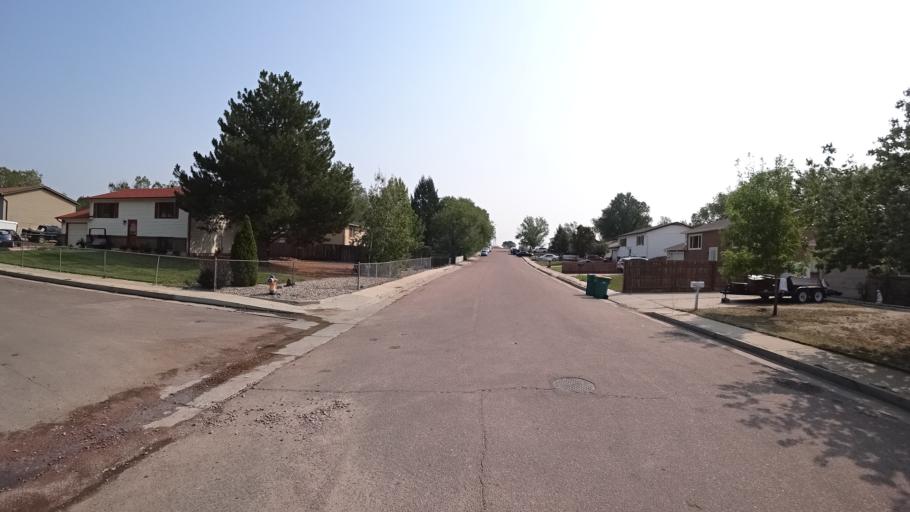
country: US
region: Colorado
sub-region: El Paso County
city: Stratmoor
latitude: 38.8097
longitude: -104.7611
